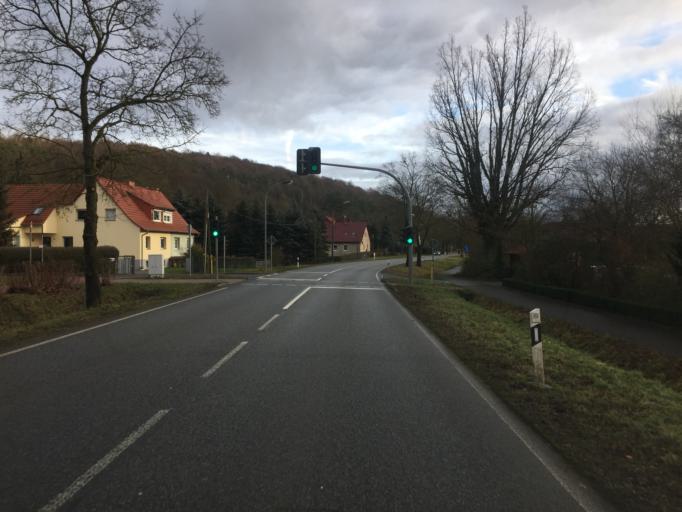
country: DE
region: Thuringia
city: Haynrode
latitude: 51.4140
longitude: 10.4600
